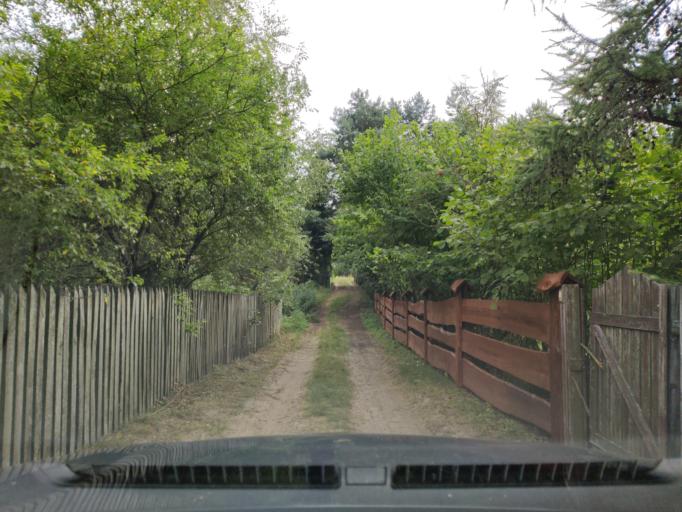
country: PL
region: Masovian Voivodeship
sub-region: Powiat pultuski
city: Pultusk
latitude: 52.7633
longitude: 21.1387
